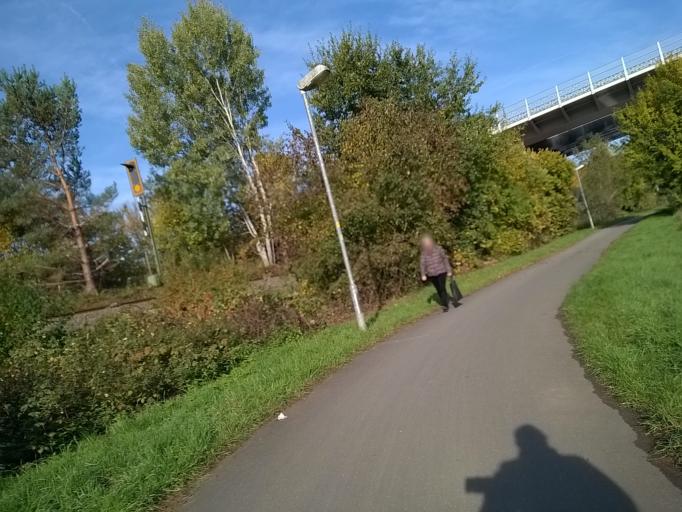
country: DE
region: Rheinland-Pfalz
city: Kaiserslautern
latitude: 49.4548
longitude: 7.7459
